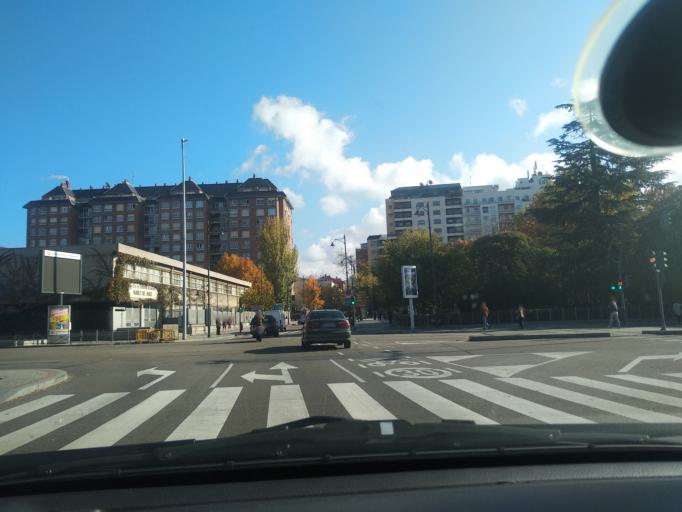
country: ES
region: Castille and Leon
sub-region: Provincia de Valladolid
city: Valladolid
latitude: 41.6536
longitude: -4.7327
